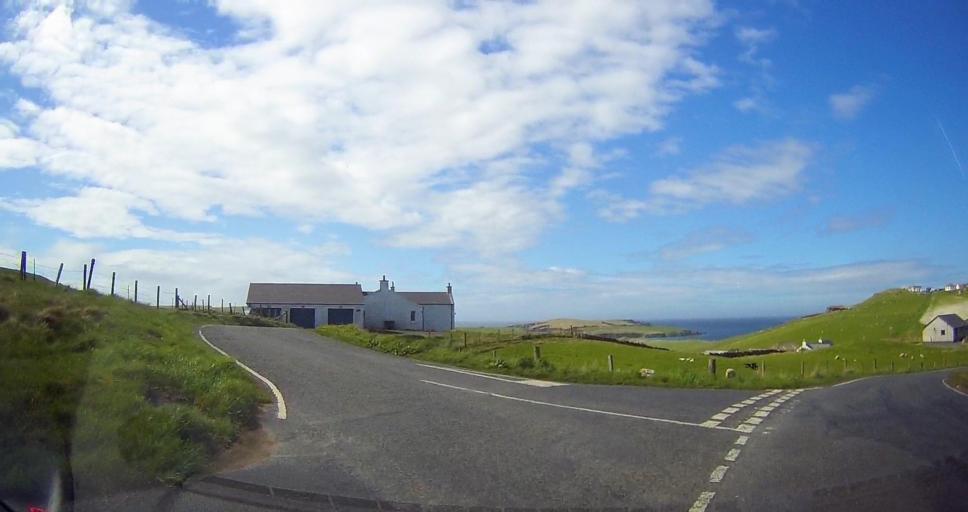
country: GB
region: Scotland
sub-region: Shetland Islands
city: Sandwick
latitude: 59.9391
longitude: -1.3231
